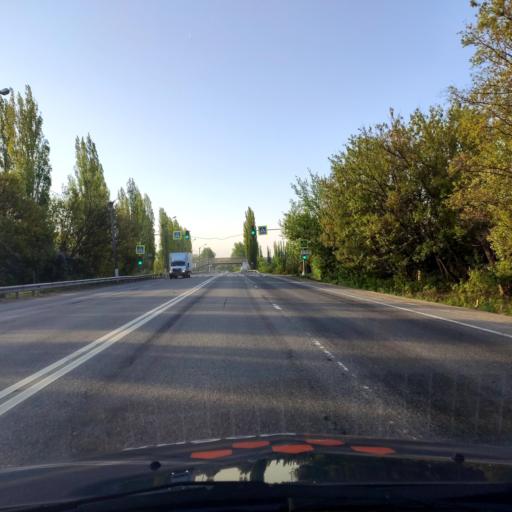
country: RU
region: Lipetsk
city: Yelets
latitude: 52.6026
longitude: 38.4705
